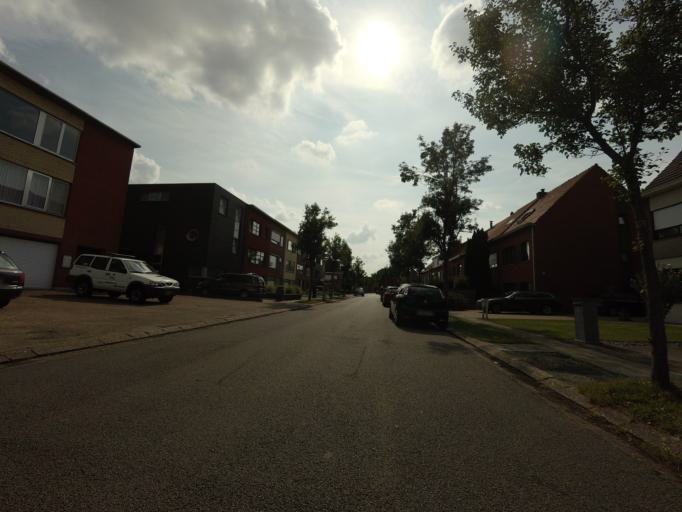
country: BE
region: Flanders
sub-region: Provincie Antwerpen
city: Aartselaar
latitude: 51.1389
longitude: 4.3847
